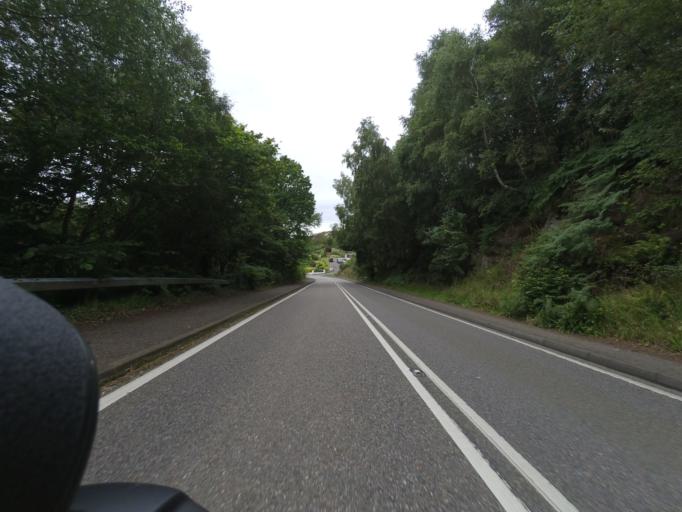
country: GB
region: Scotland
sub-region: Highland
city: Ullapool
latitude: 57.8943
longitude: -5.1435
